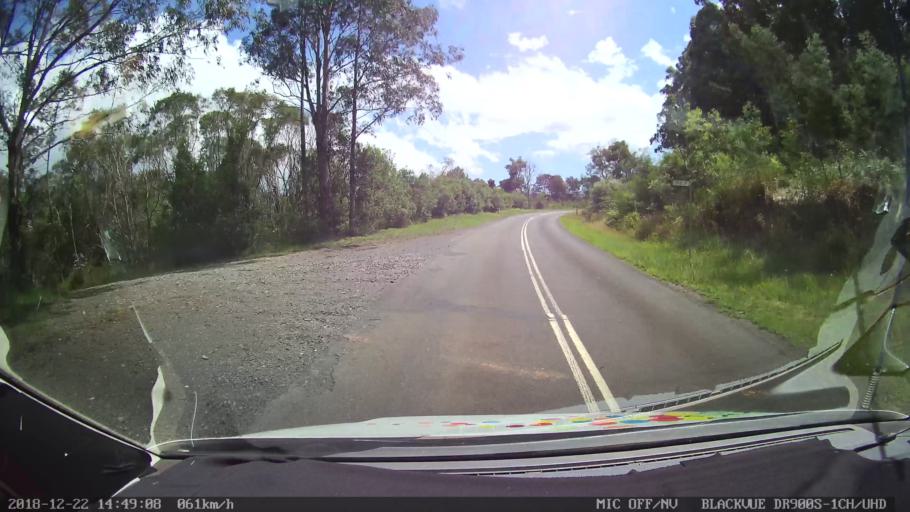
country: AU
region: New South Wales
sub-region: Bellingen
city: Dorrigo
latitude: -30.1871
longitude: 152.5506
